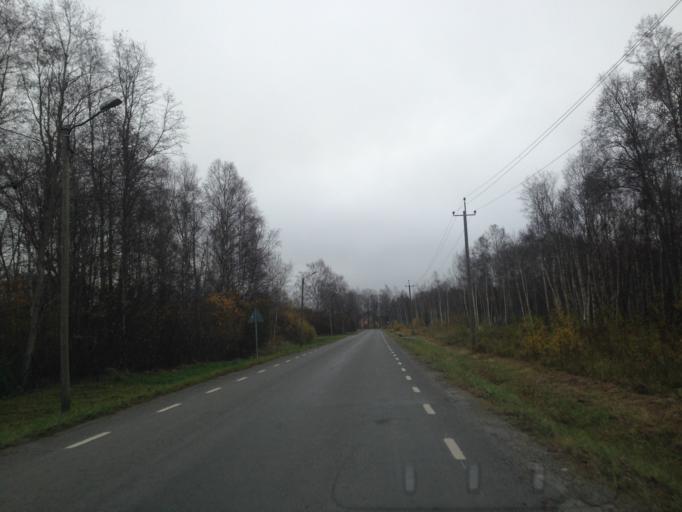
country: EE
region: Harju
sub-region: Harku vald
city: Tabasalu
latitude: 59.3759
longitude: 24.5396
